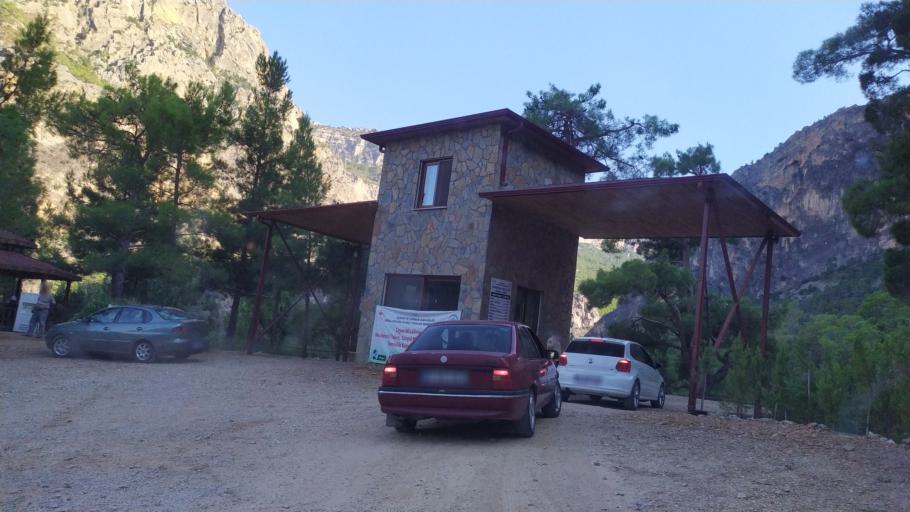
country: TR
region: Mersin
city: Mut
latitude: 36.5432
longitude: 33.2326
